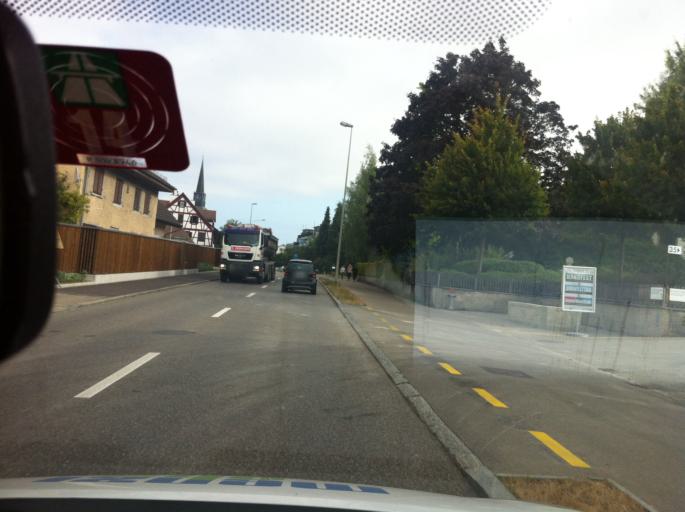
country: CH
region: Zurich
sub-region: Bezirk Buelach
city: Buelach / Seematt
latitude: 47.5136
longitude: 8.5431
